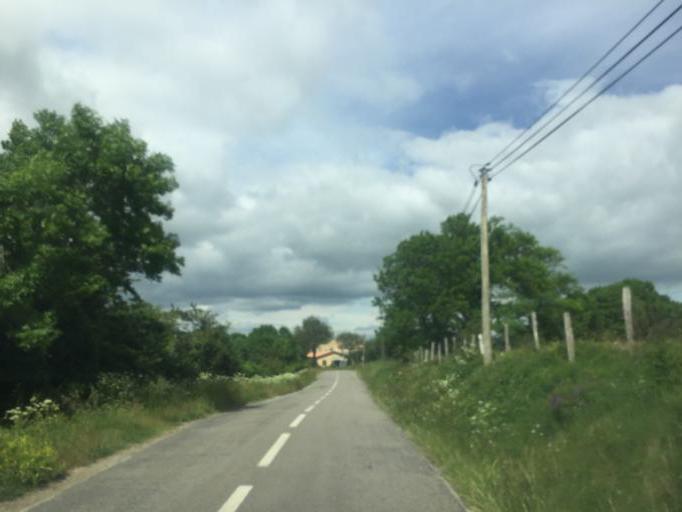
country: FR
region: Rhone-Alpes
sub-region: Departement de l'Ardeche
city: Saint-Priest
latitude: 44.6594
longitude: 4.5648
